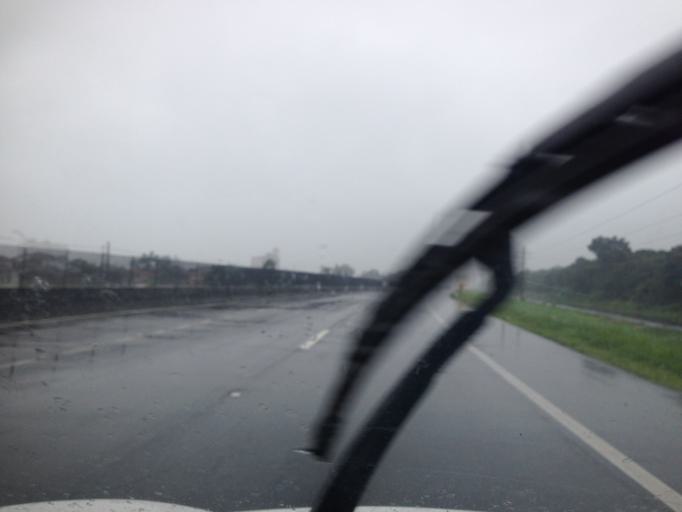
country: BR
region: Sao Paulo
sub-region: Mongagua
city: Mongagua
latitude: -24.0663
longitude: -46.5711
